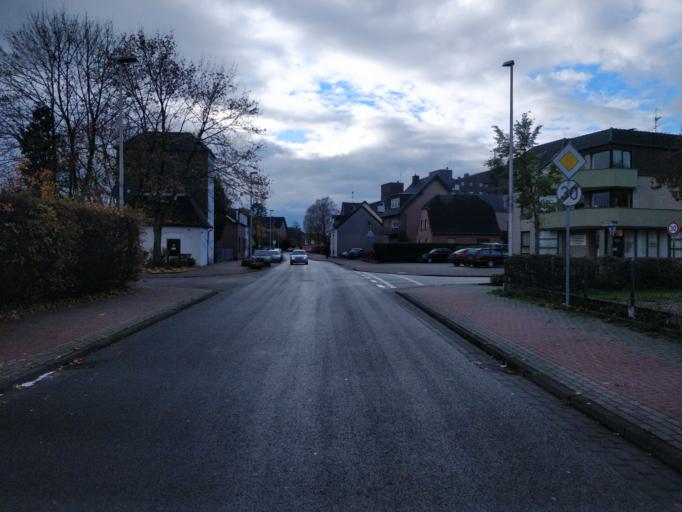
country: DE
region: North Rhine-Westphalia
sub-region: Regierungsbezirk Dusseldorf
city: Emmerich
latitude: 51.8482
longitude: 6.2562
